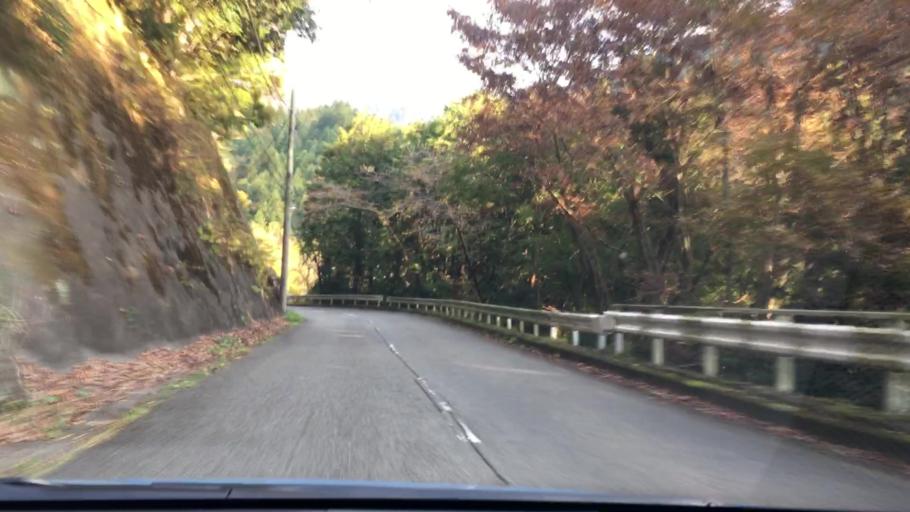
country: JP
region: Yamanashi
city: Uenohara
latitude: 35.5593
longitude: 139.1670
